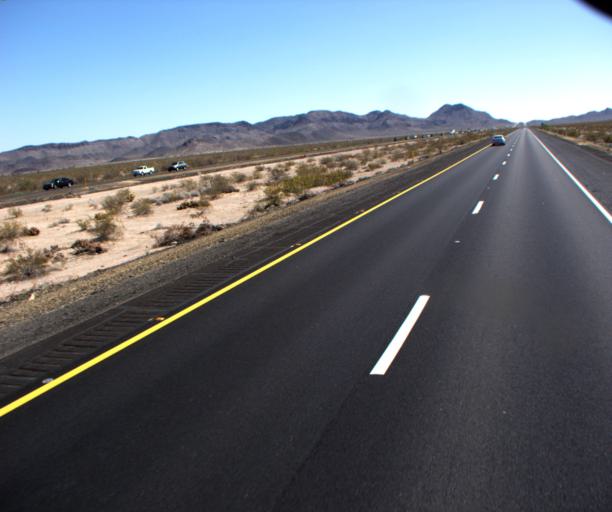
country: US
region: Arizona
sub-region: La Paz County
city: Salome
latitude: 33.6195
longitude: -113.6916
